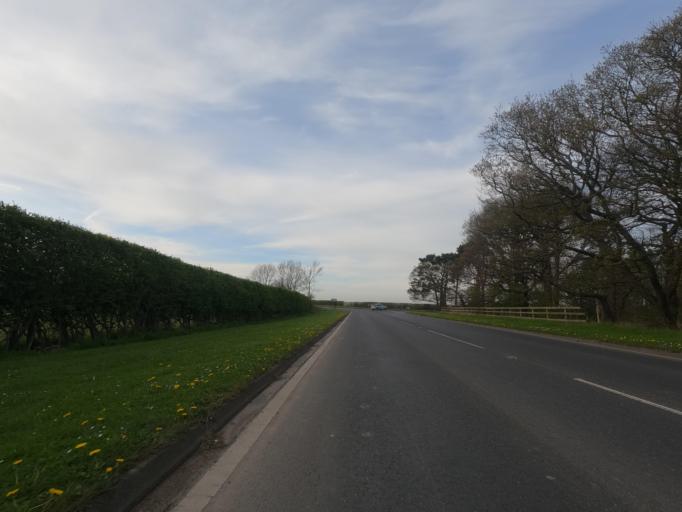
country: GB
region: England
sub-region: Newcastle upon Tyne
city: Dinnington
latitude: 55.0405
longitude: -1.6675
